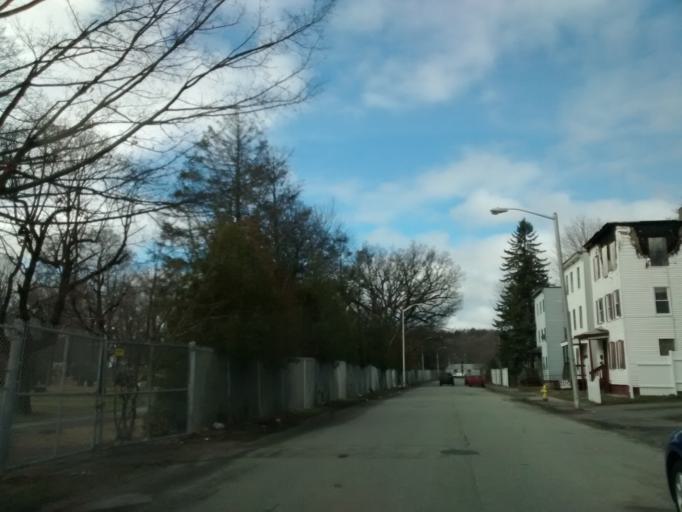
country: US
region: Massachusetts
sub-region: Worcester County
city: Worcester
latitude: 42.2822
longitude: -71.8028
